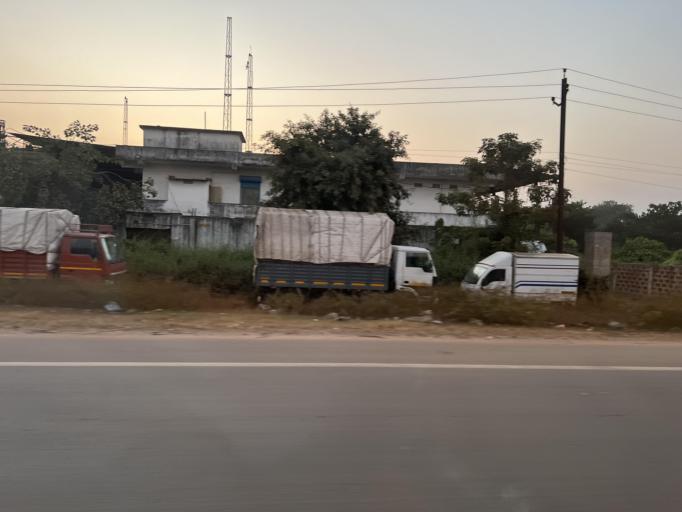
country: IN
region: Odisha
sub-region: Cuttack
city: Cuttack
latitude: 20.3832
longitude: 85.8882
